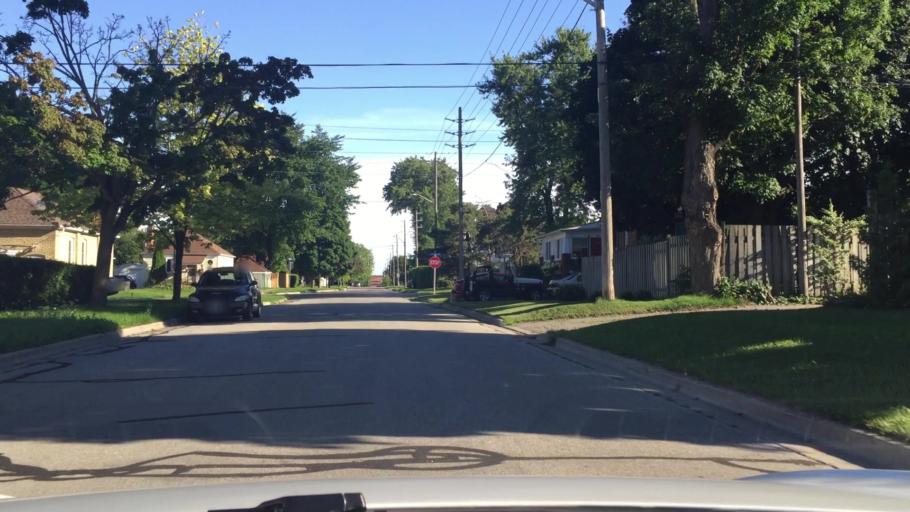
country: CA
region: Ontario
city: Oshawa
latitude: 43.9001
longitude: -78.8837
